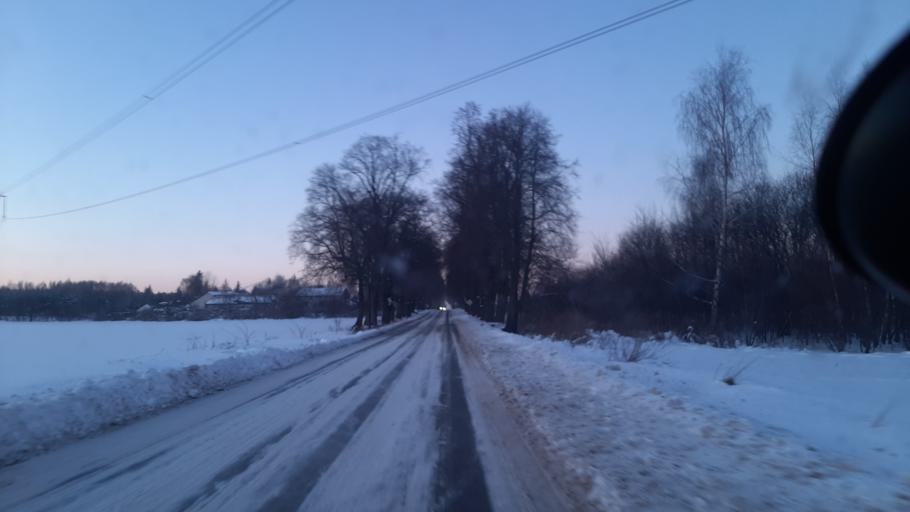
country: PL
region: Lublin Voivodeship
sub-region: Powiat lubelski
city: Lublin
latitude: 51.3305
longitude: 22.5561
